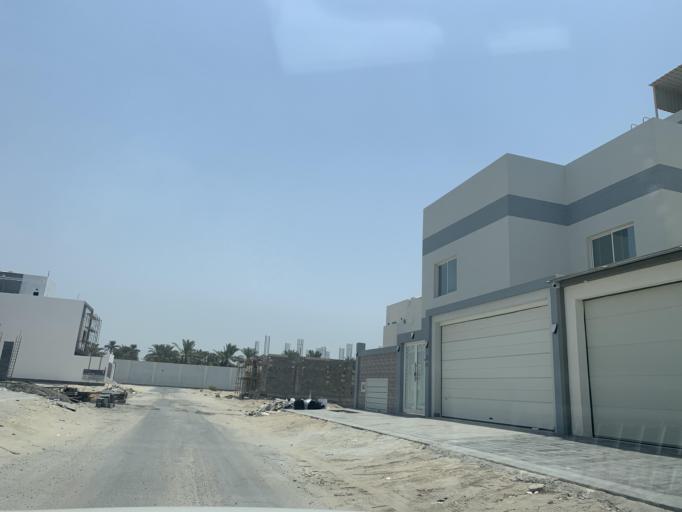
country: BH
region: Manama
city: Jidd Hafs
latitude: 26.2139
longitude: 50.4697
